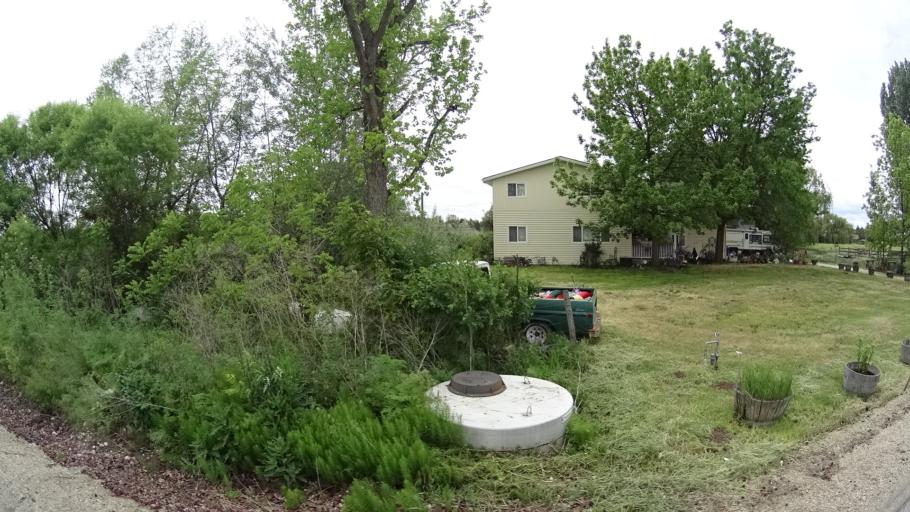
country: US
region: Idaho
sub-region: Ada County
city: Star
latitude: 43.6914
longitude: -116.4275
